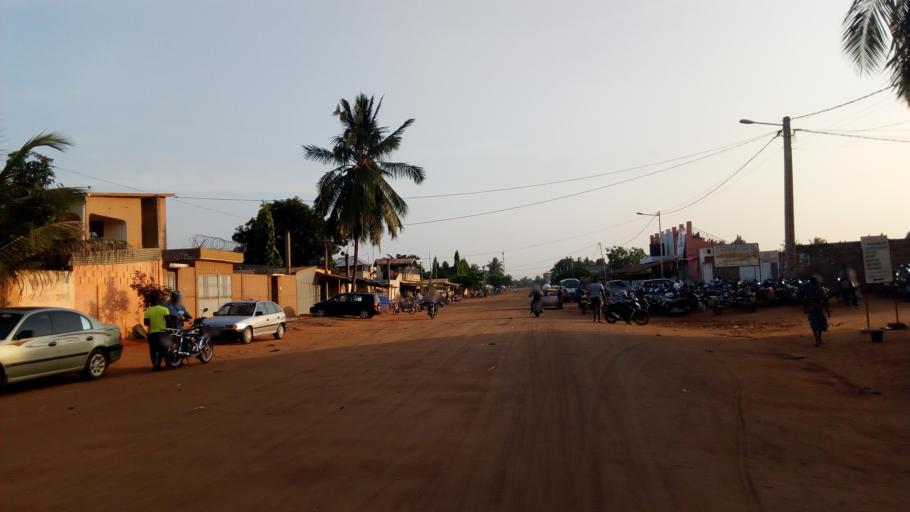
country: TG
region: Maritime
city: Lome
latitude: 6.1848
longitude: 1.1782
